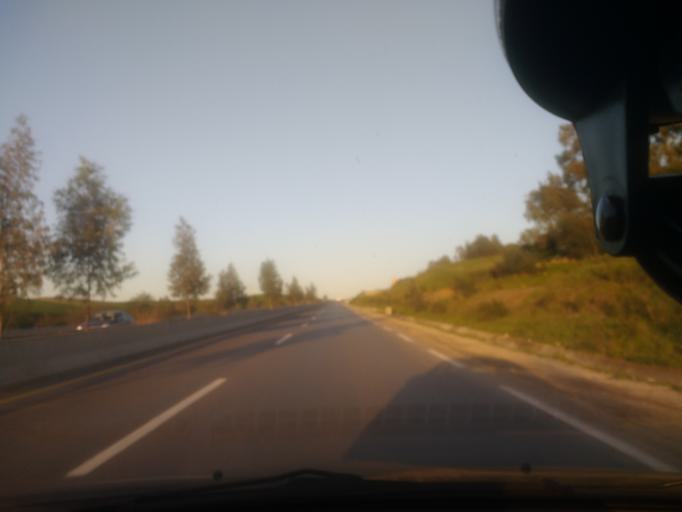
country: DZ
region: Boumerdes
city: Makouda
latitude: 36.7563
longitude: 4.0419
